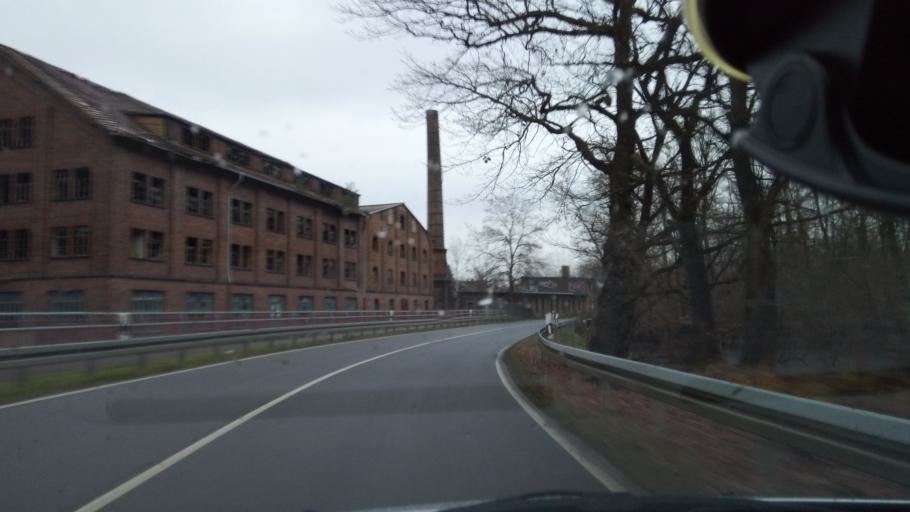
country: DE
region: Saxony-Anhalt
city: Muldenstein
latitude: 51.6602
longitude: 12.3470
